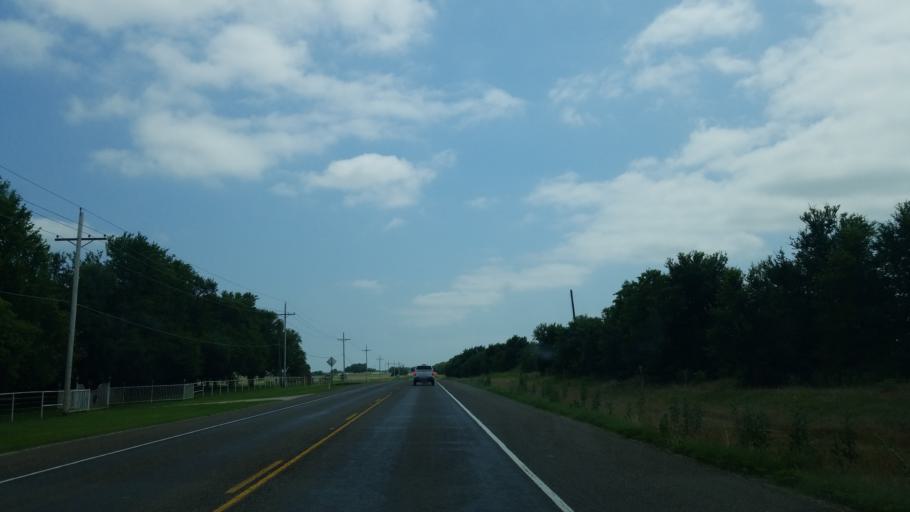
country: US
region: Texas
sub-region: Denton County
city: Aubrey
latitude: 33.3398
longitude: -96.9694
